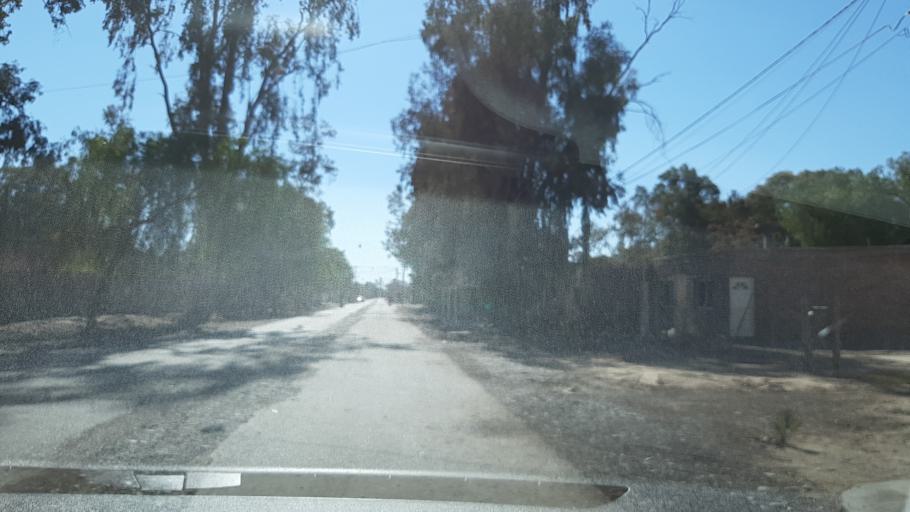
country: AR
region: San Juan
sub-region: Departamento de Zonda
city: Zonda
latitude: -31.5521
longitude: -68.7291
